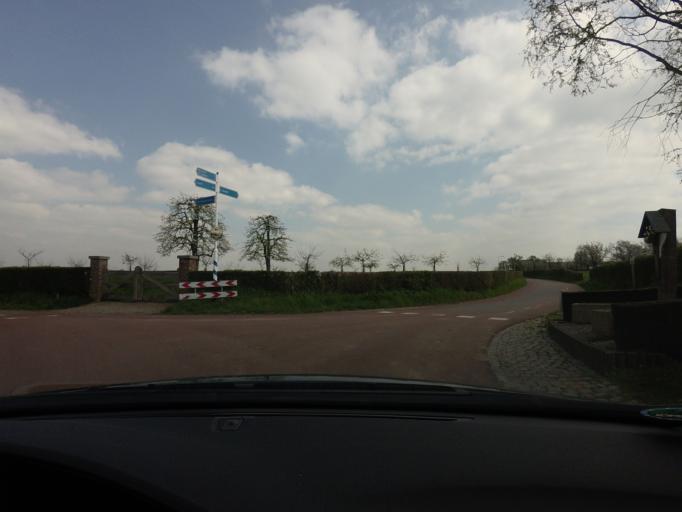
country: NL
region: Limburg
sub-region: Eijsden-Margraten
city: Eijsden
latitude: 50.7839
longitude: 5.7588
